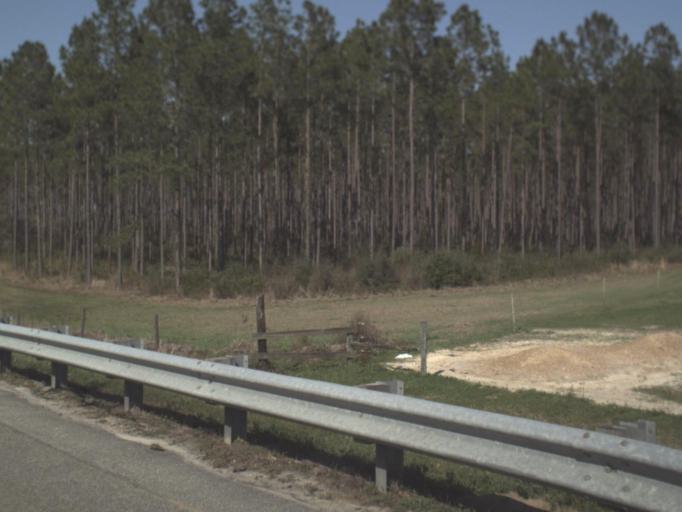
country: US
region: Florida
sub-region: Gulf County
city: Wewahitchka
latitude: 30.1527
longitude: -85.2094
